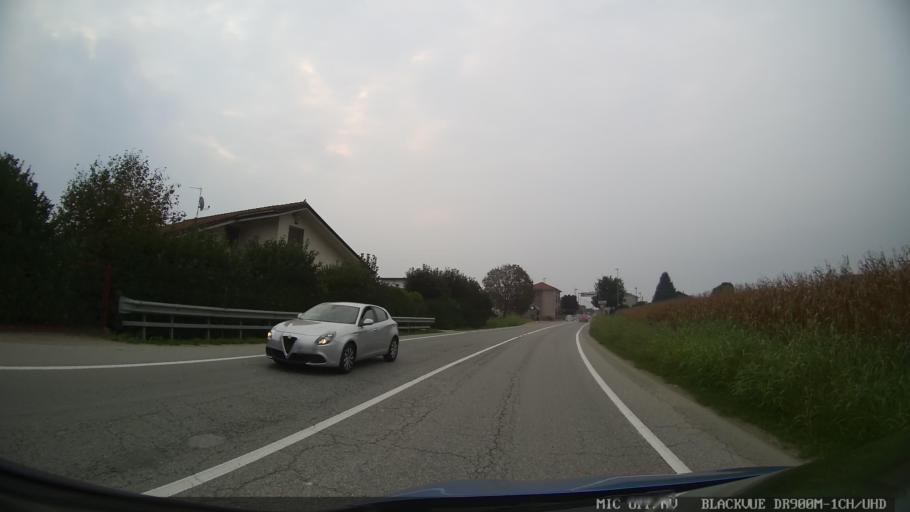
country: IT
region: Piedmont
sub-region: Provincia di Torino
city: Carmagnola
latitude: 44.8698
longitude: 7.7119
